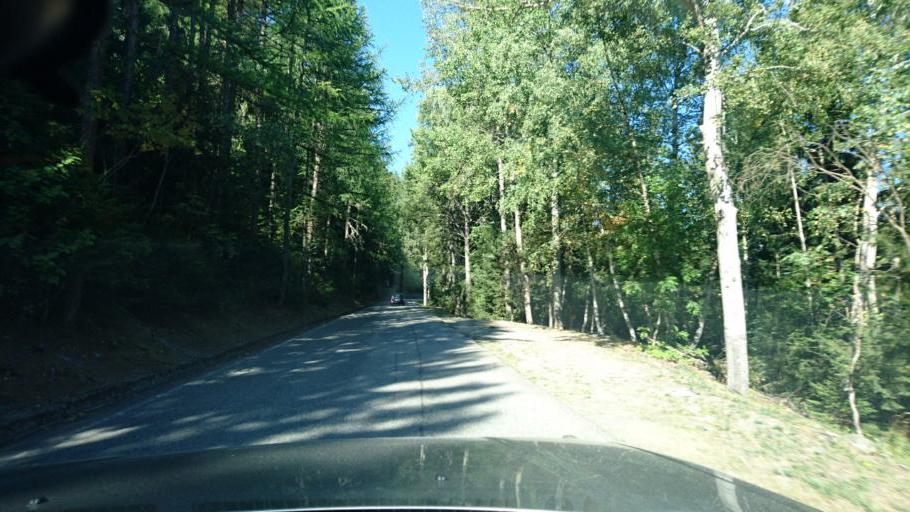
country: IT
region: Aosta Valley
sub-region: Valle d'Aosta
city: Morgex
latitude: 45.7444
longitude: 7.0387
